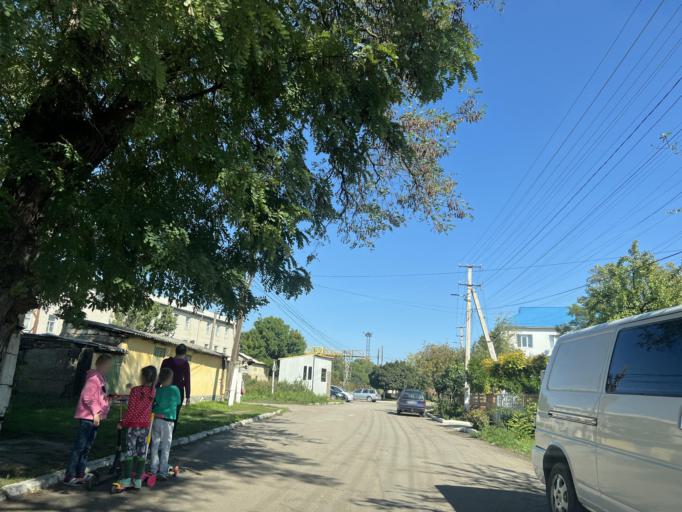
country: MD
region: Ungheni
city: Ungheni
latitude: 47.2022
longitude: 27.8007
